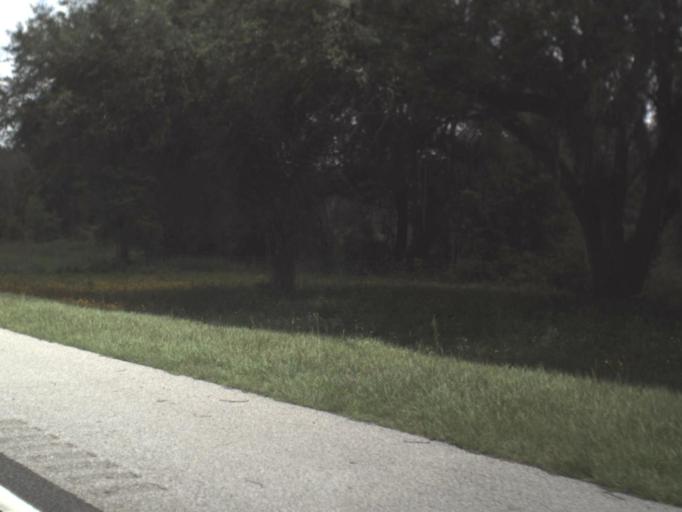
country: US
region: Florida
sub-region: Suwannee County
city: Wellborn
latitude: 30.3091
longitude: -82.7982
